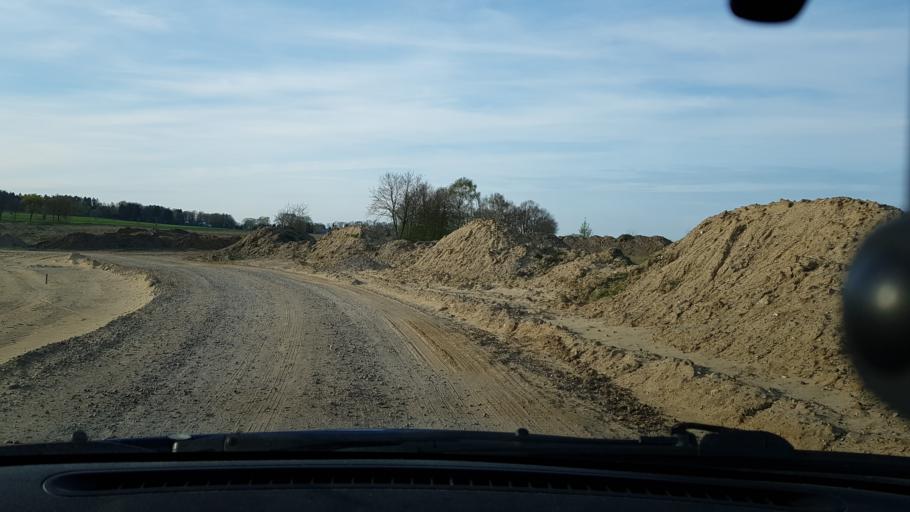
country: DE
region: Lower Saxony
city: Buchholz in der Nordheide
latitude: 53.3582
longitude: 9.8728
